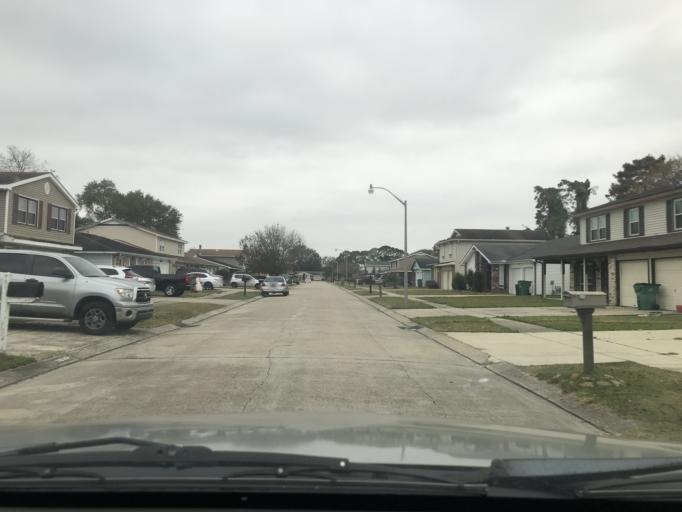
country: US
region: Louisiana
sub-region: Jefferson Parish
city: Woodmere
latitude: 29.8608
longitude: -90.0761
